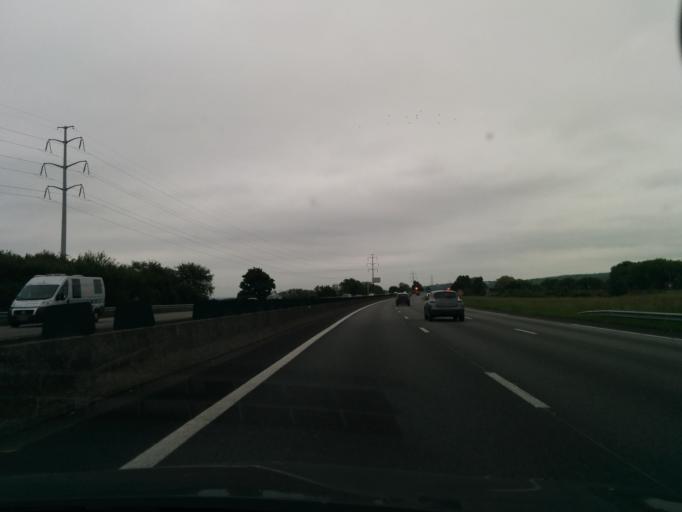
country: FR
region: Ile-de-France
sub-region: Departement des Yvelines
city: Epone
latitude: 48.9657
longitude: 1.8123
